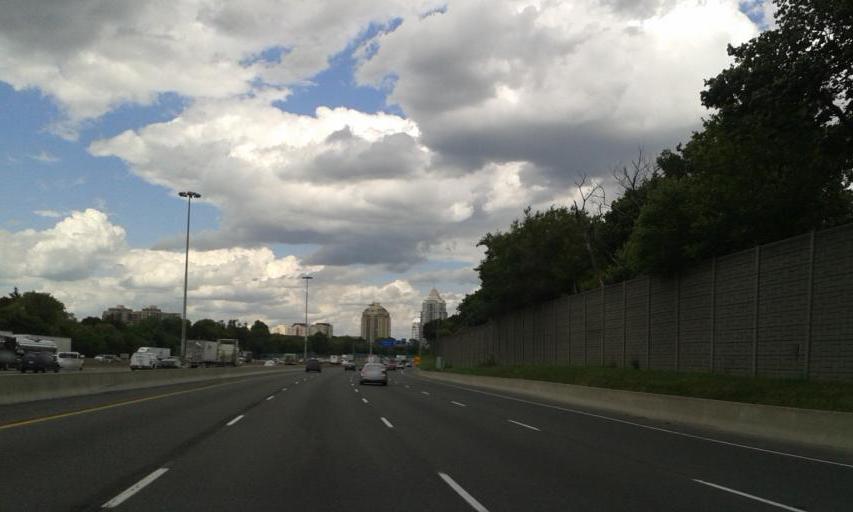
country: CA
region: Ontario
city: Willowdale
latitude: 43.7591
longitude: -79.3983
